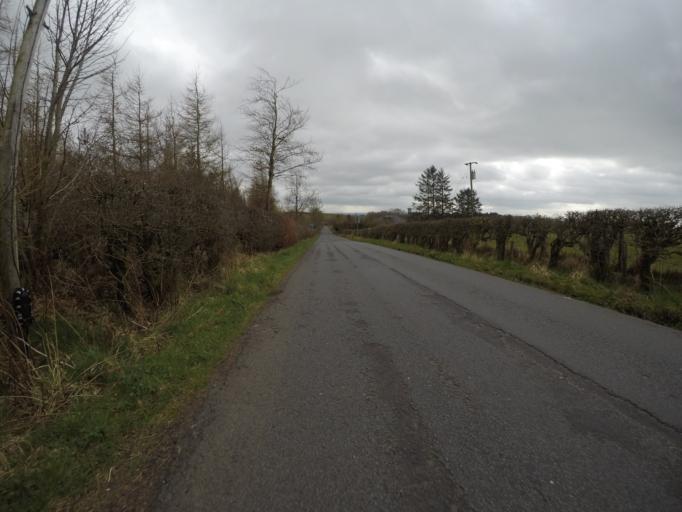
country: GB
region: Scotland
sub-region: East Ayrshire
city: Stewarton
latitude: 55.6751
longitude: -4.4394
